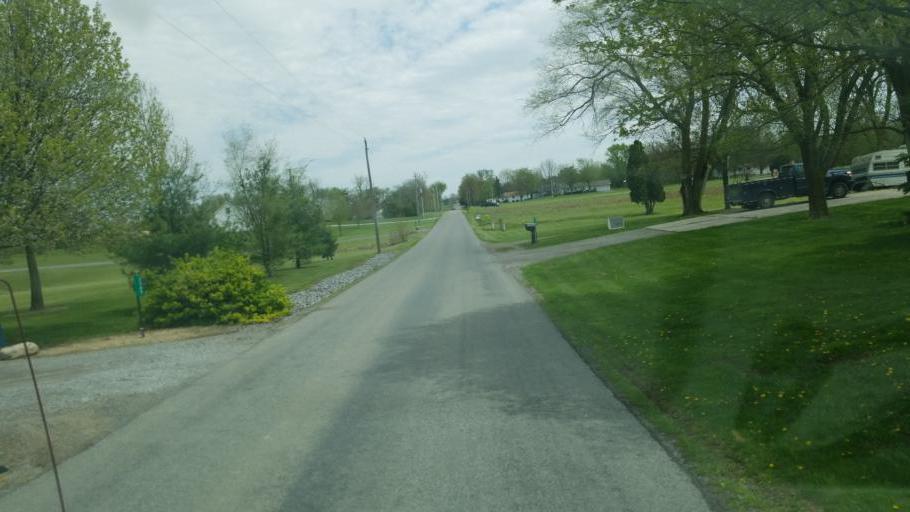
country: US
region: Ohio
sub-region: Allen County
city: Bluffton
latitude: 40.8115
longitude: -83.9597
